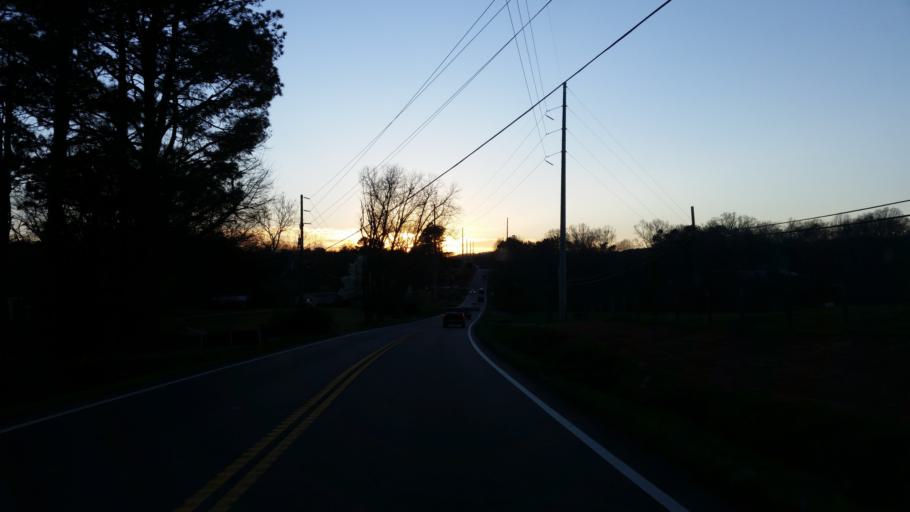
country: US
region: Georgia
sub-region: Hall County
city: Flowery Branch
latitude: 34.2913
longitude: -84.0119
